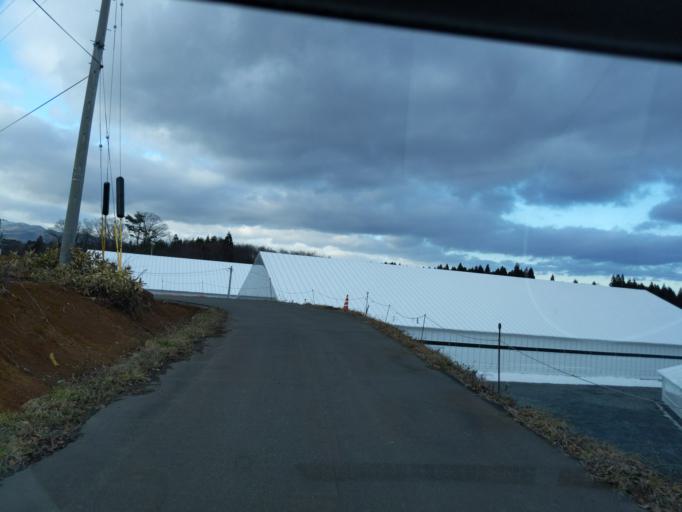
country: JP
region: Iwate
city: Ichinoseki
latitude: 38.9759
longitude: 141.0145
